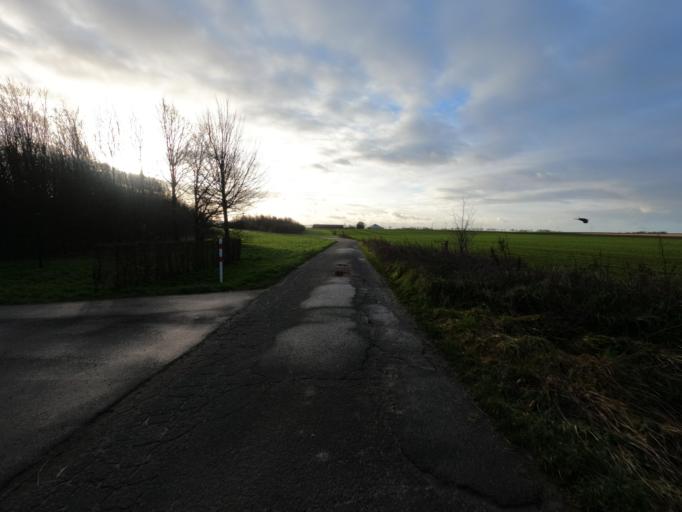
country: DE
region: North Rhine-Westphalia
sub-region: Regierungsbezirk Koln
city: Heinsberg
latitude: 51.0670
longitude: 6.0675
